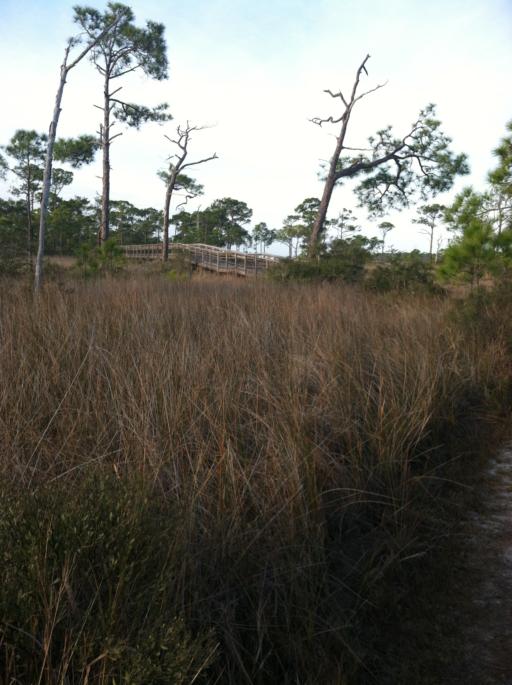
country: US
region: Florida
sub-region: Franklin County
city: Eastpoint
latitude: 29.7102
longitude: -84.7596
